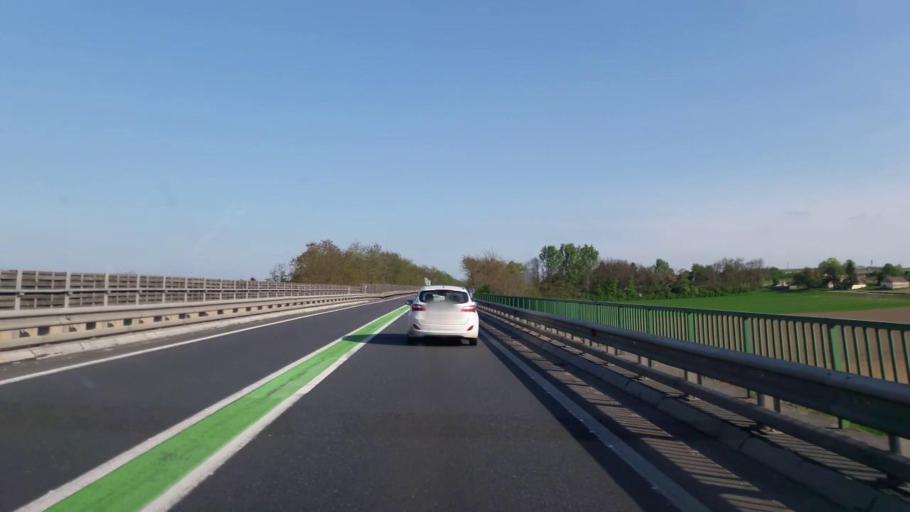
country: AT
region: Lower Austria
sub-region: Politischer Bezirk Hollabrunn
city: Gollersdorf
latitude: 48.5046
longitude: 16.0999
